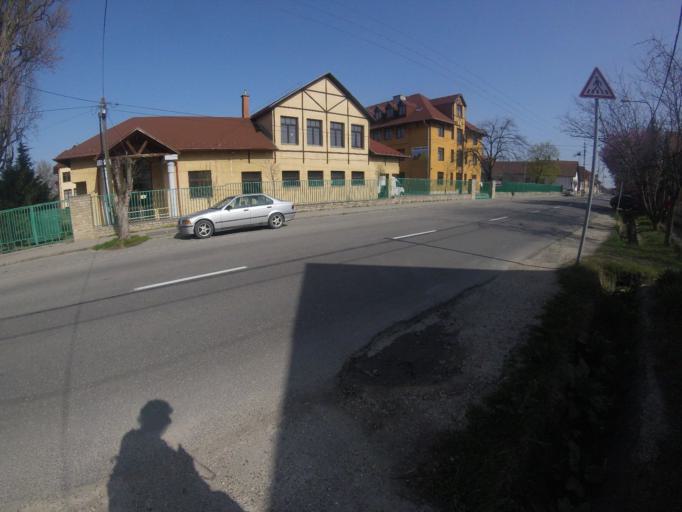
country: HU
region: Pest
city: Pilisvorosvar
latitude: 47.6209
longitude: 18.9026
